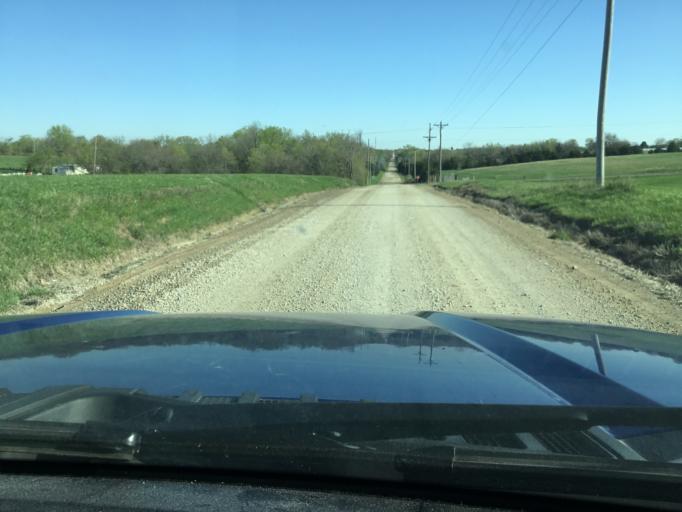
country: US
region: Kansas
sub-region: Douglas County
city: Lawrence
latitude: 38.9698
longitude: -95.3538
